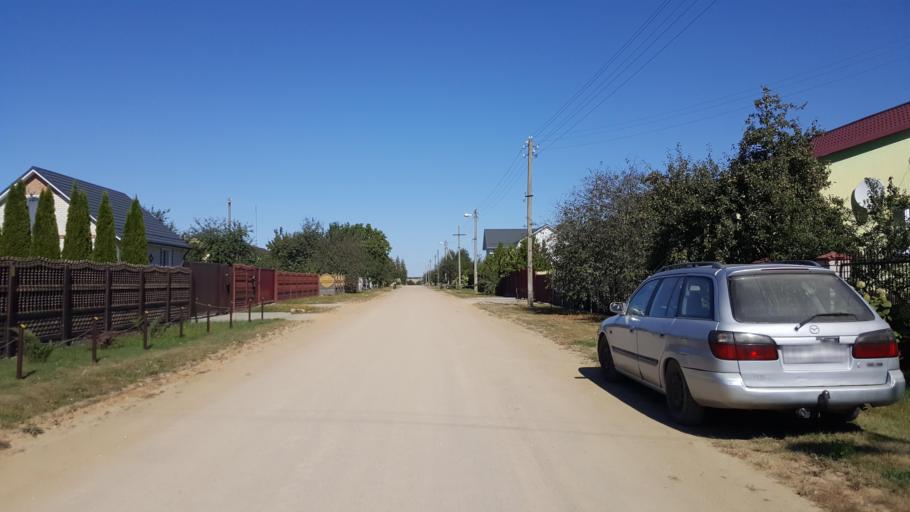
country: BY
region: Brest
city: Vysokaye
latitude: 52.2607
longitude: 23.5019
